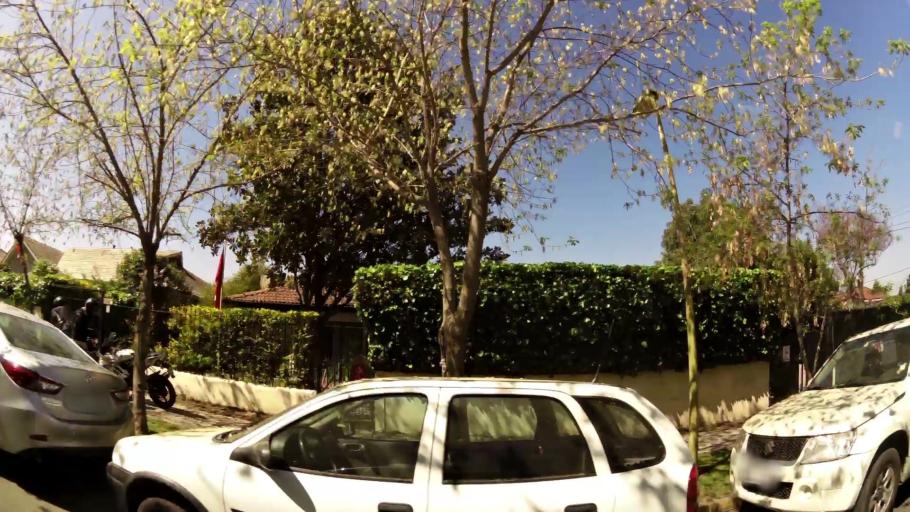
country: CL
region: Santiago Metropolitan
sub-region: Provincia de Santiago
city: Villa Presidente Frei, Nunoa, Santiago, Chile
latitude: -33.4267
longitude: -70.5627
